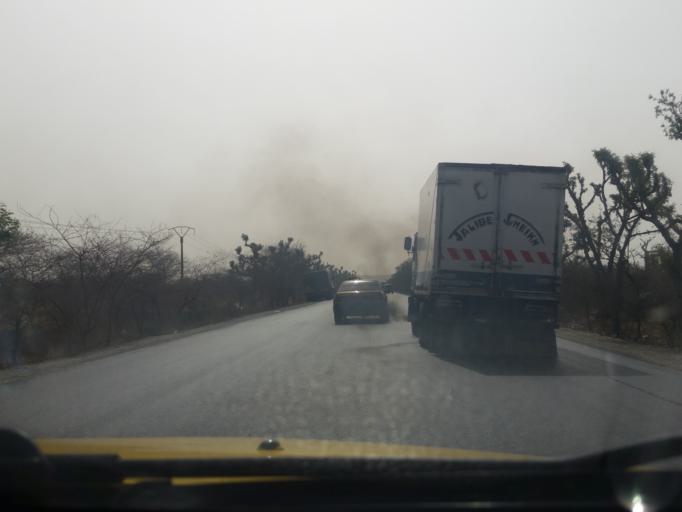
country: SN
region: Thies
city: Pout
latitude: 14.7630
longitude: -17.0250
